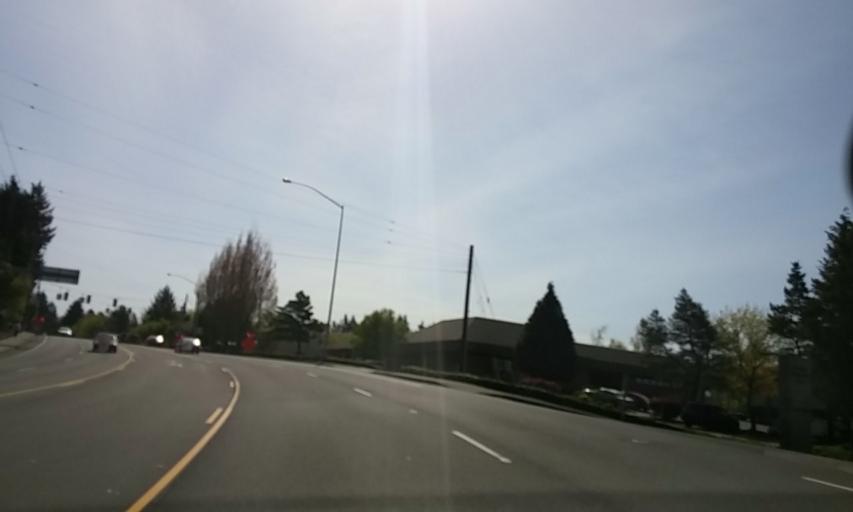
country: US
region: Oregon
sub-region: Washington County
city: West Haven-Sylvan
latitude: 45.5094
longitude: -122.7744
